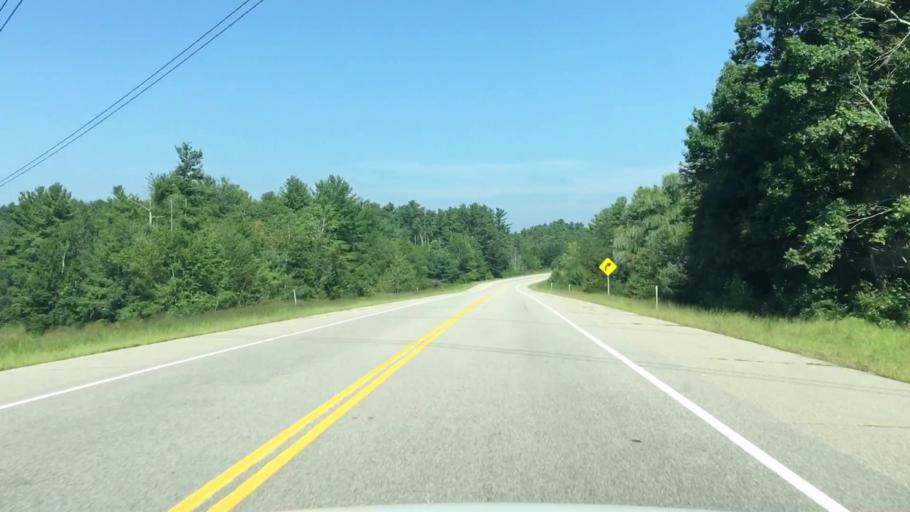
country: US
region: New Hampshire
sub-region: Rockingham County
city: Seabrook
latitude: 42.9003
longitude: -70.9070
